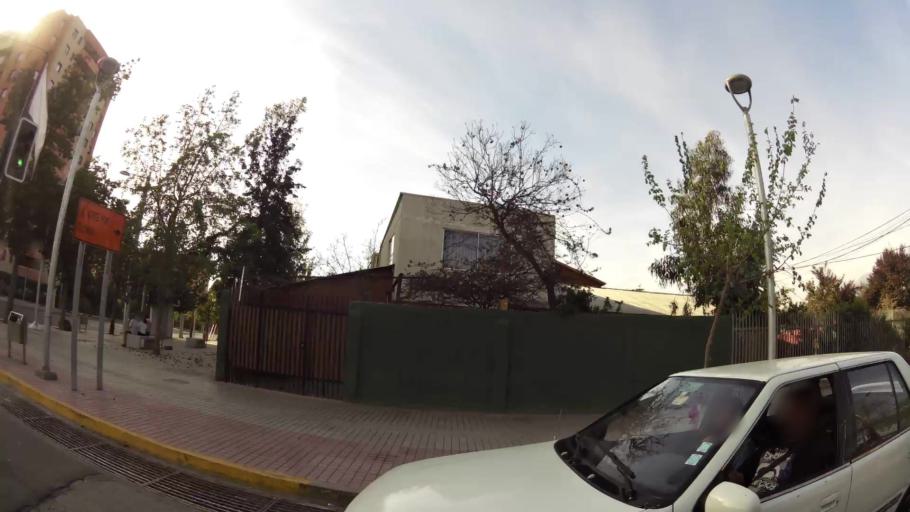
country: CL
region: Santiago Metropolitan
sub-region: Provincia de Santiago
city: Villa Presidente Frei, Nunoa, Santiago, Chile
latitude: -33.5282
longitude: -70.5879
